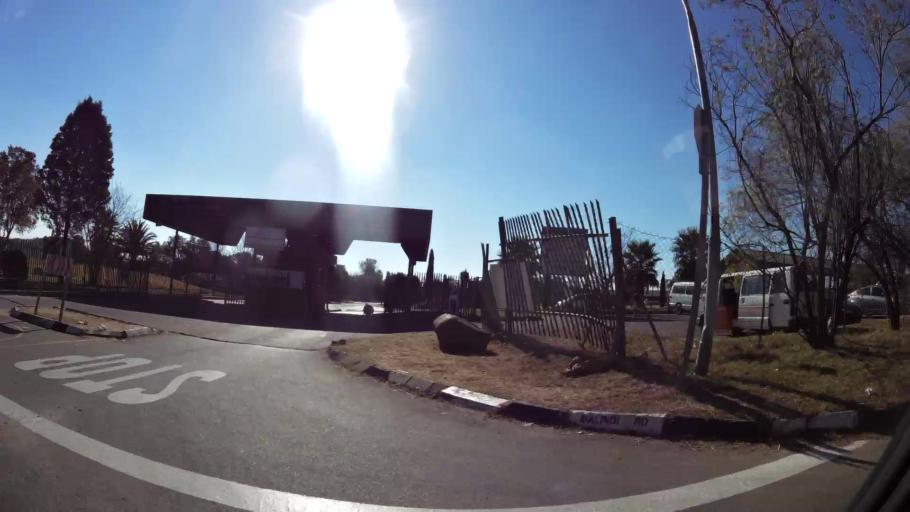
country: ZA
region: Gauteng
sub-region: City of Johannesburg Metropolitan Municipality
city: Midrand
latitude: -26.0207
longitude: 28.0623
